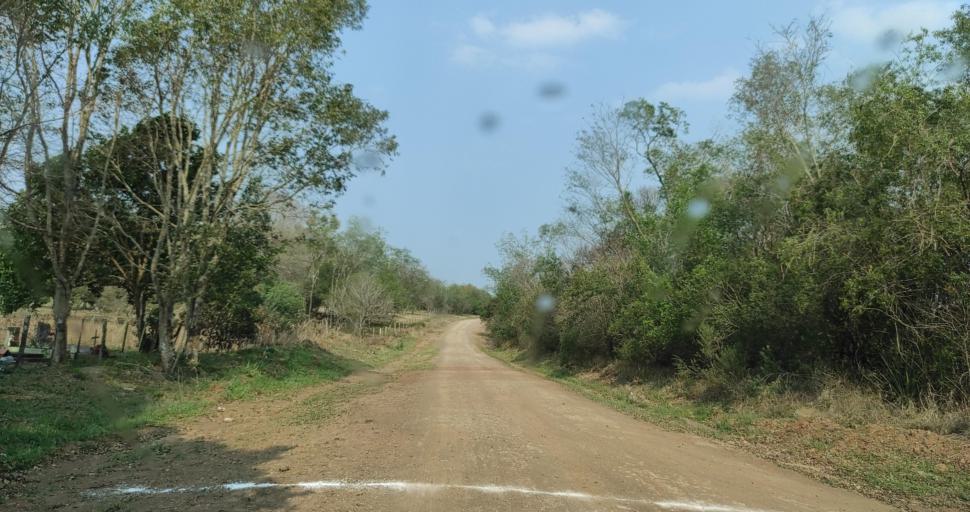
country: AR
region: Misiones
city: Cerro Azul
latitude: -27.5970
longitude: -55.5766
